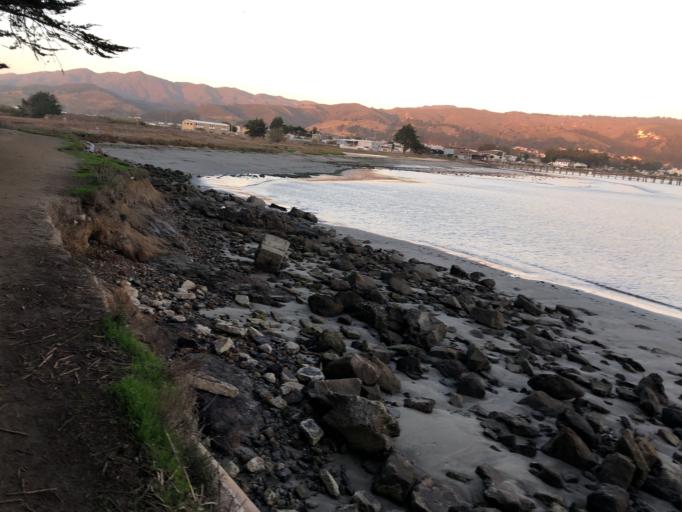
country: US
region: California
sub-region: San Mateo County
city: El Granada
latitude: 37.4995
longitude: -122.4960
